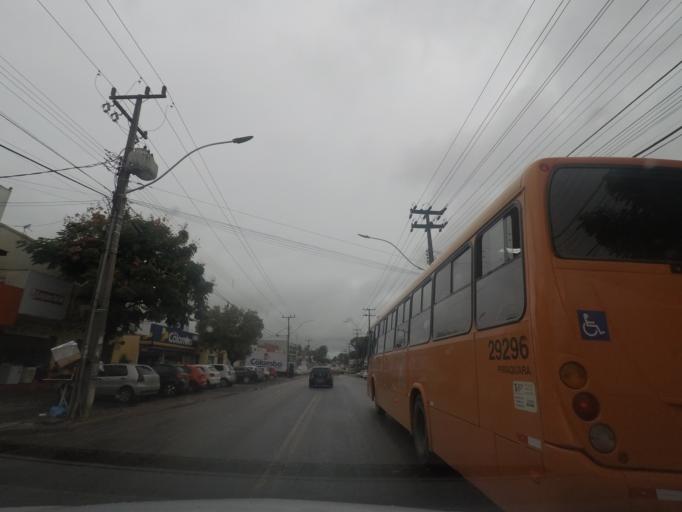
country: BR
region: Parana
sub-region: Piraquara
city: Piraquara
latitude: -25.4483
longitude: -49.0669
